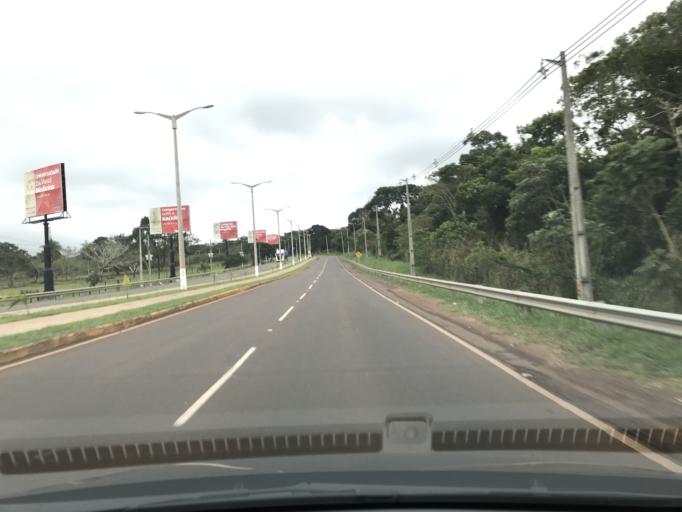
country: PY
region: Canindeyu
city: Salto del Guaira
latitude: -24.0400
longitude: -54.3129
